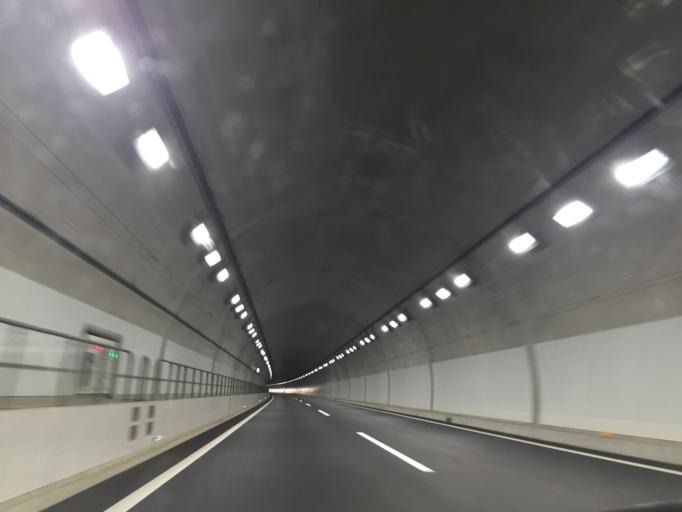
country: JP
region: Aichi
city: Shinshiro
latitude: 34.9155
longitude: 137.4766
